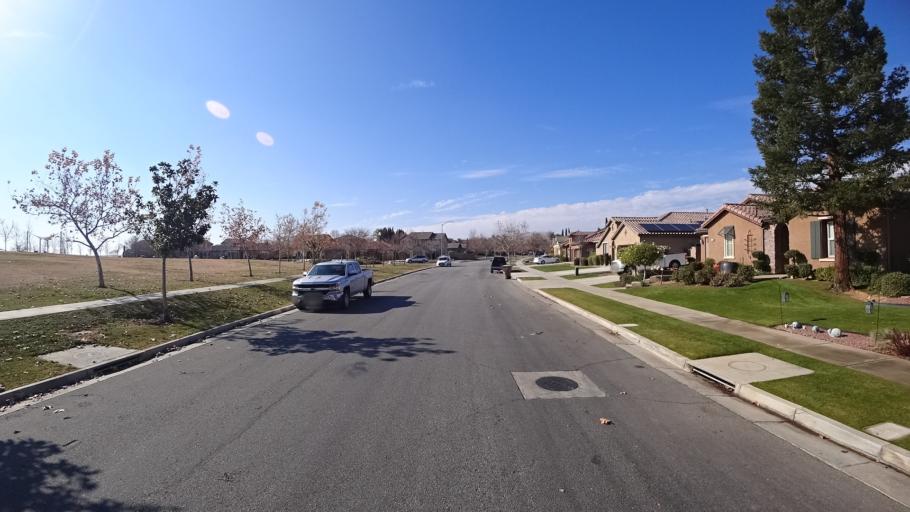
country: US
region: California
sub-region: Kern County
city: Oildale
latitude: 35.4035
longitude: -118.8930
